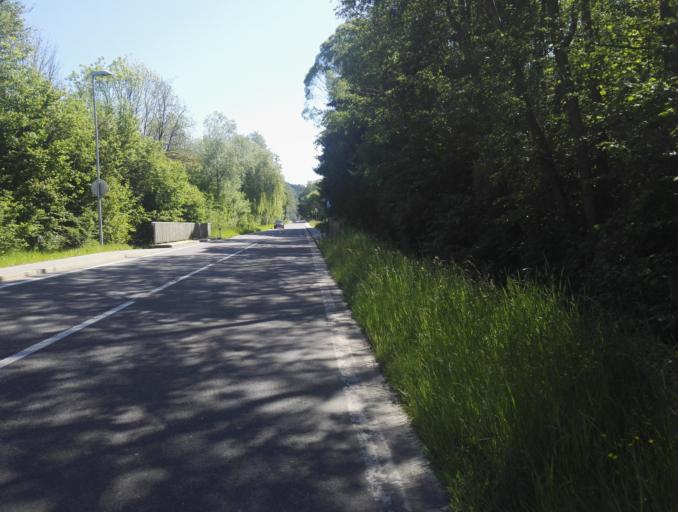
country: AT
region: Styria
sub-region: Politischer Bezirk Graz-Umgebung
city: Hart bei Graz
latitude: 47.0618
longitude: 15.5537
